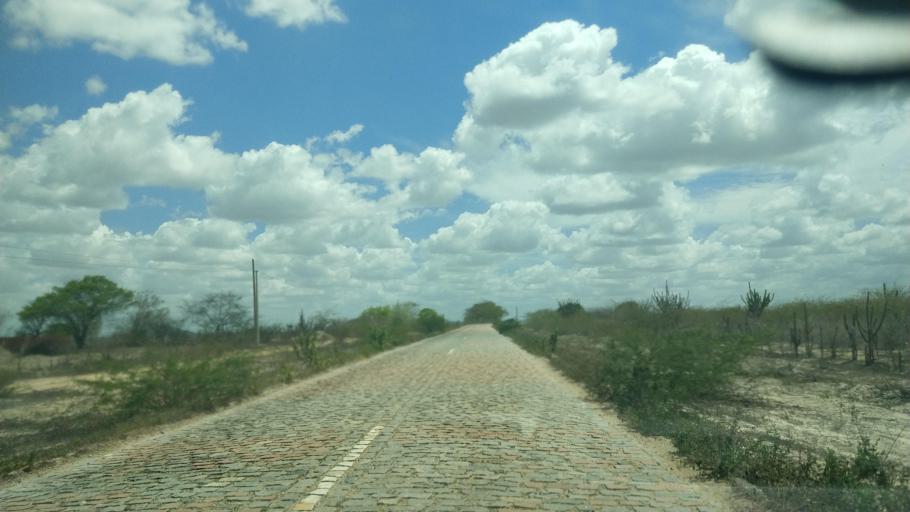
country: BR
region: Rio Grande do Norte
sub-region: Sao Paulo Do Potengi
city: Sao Paulo do Potengi
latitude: -5.9550
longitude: -35.8466
